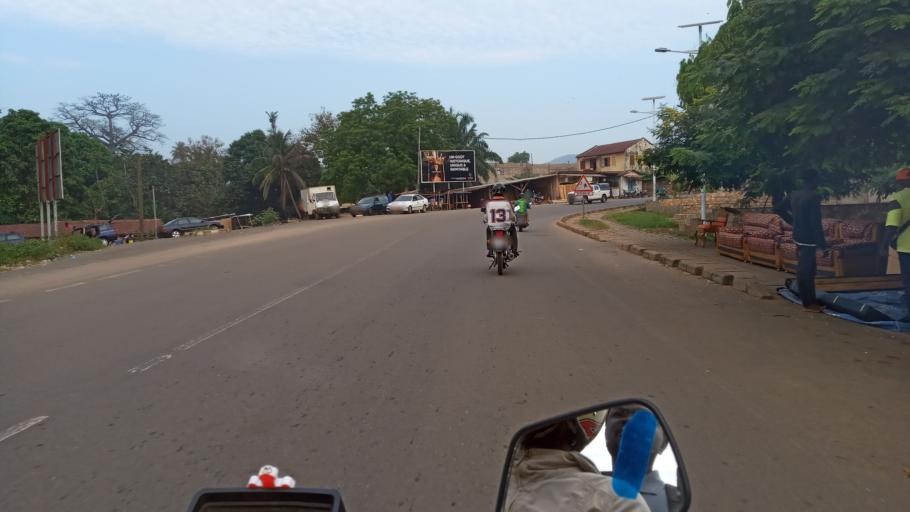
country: TG
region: Plateaux
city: Kpalime
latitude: 6.9041
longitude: 0.6320
